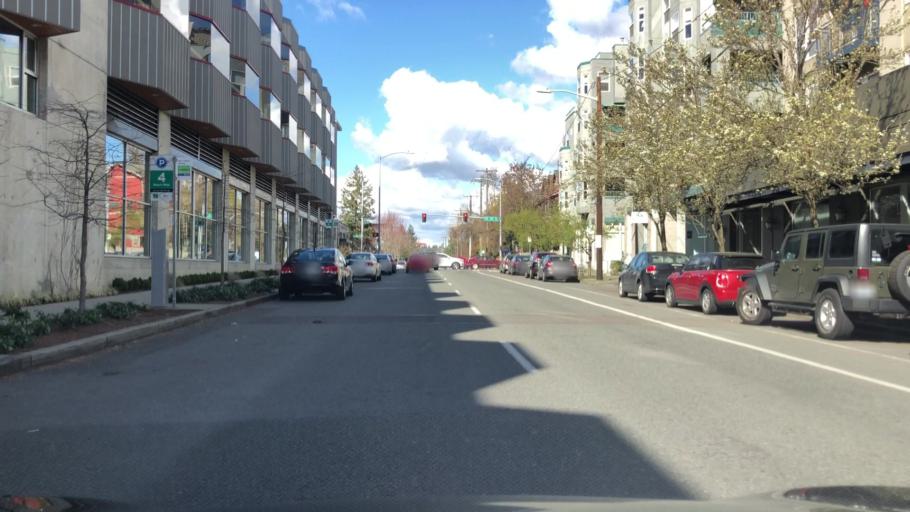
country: US
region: Washington
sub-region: King County
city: Seattle
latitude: 47.6641
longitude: -122.3164
